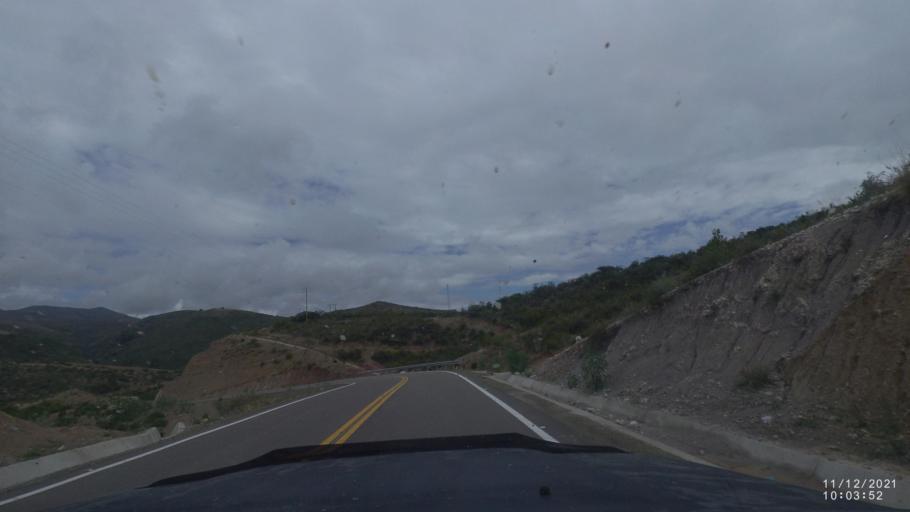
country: BO
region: Cochabamba
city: Cliza
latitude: -17.7139
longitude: -65.9402
